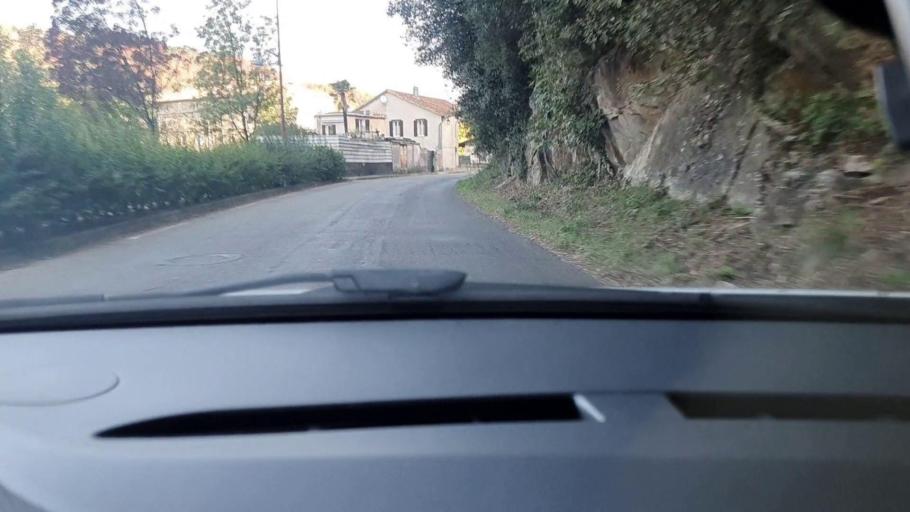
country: FR
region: Languedoc-Roussillon
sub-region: Departement du Gard
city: Besseges
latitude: 44.2967
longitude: 4.0938
